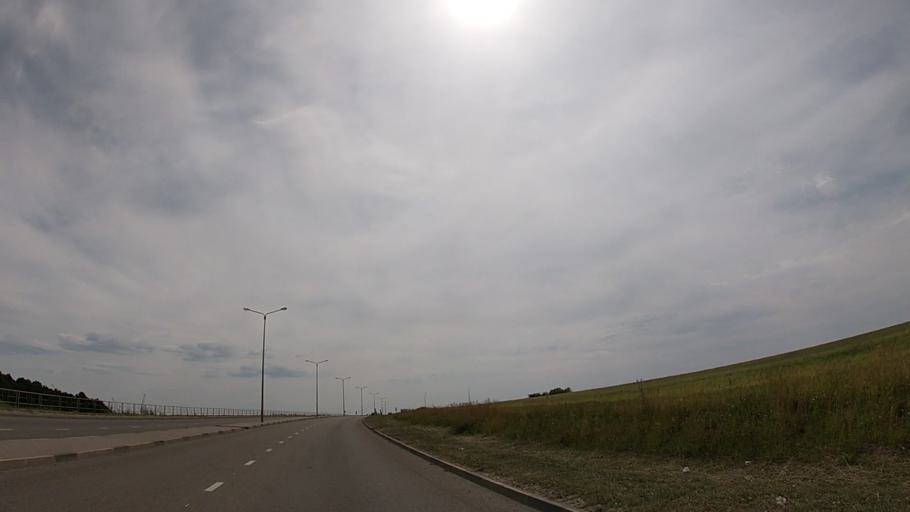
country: RU
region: Belgorod
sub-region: Belgorodskiy Rayon
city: Belgorod
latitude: 50.5948
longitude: 36.5237
